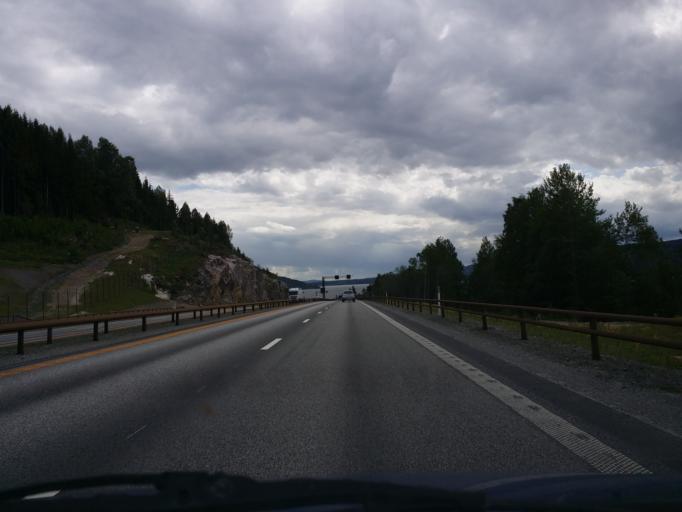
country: NO
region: Akershus
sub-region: Eidsvoll
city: Eidsvoll
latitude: 60.4914
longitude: 11.2363
